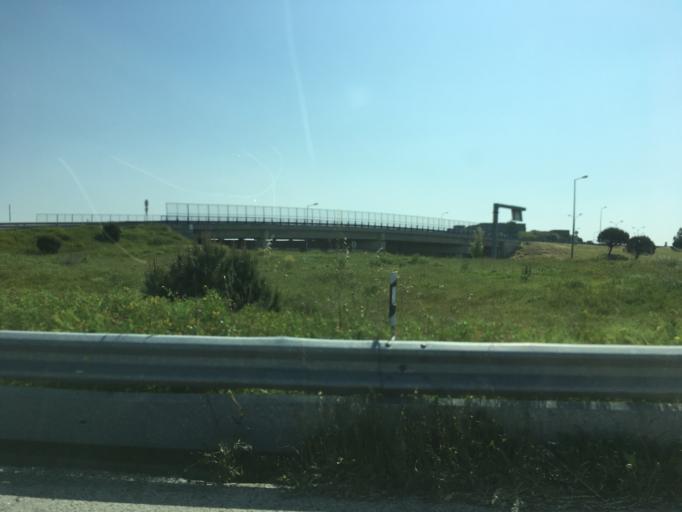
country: PT
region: Lisbon
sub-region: Sintra
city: Sintra
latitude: 38.8034
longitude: -9.3639
